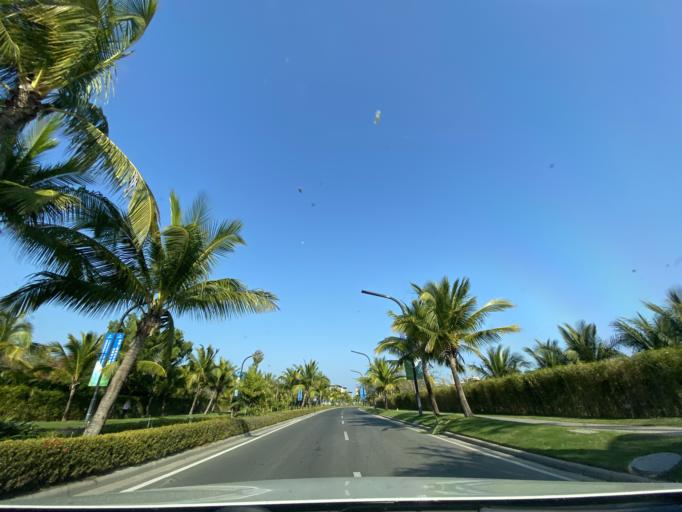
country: CN
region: Hainan
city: Xincun
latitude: 18.4236
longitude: 109.9536
